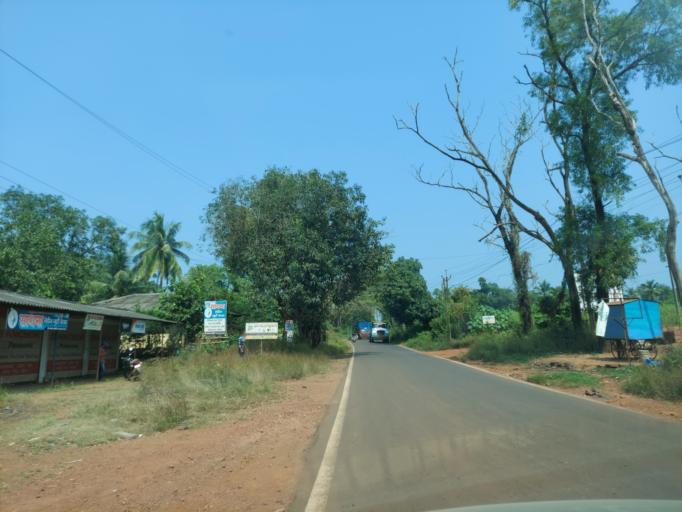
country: IN
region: Maharashtra
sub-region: Sindhudurg
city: Kudal
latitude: 15.9944
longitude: 73.6848
